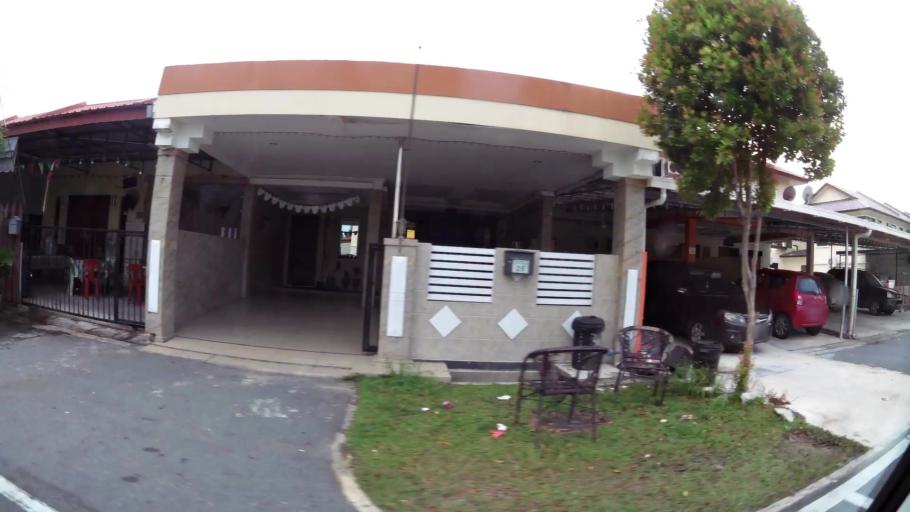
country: BN
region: Brunei and Muara
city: Bandar Seri Begawan
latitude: 4.9929
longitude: 114.9889
